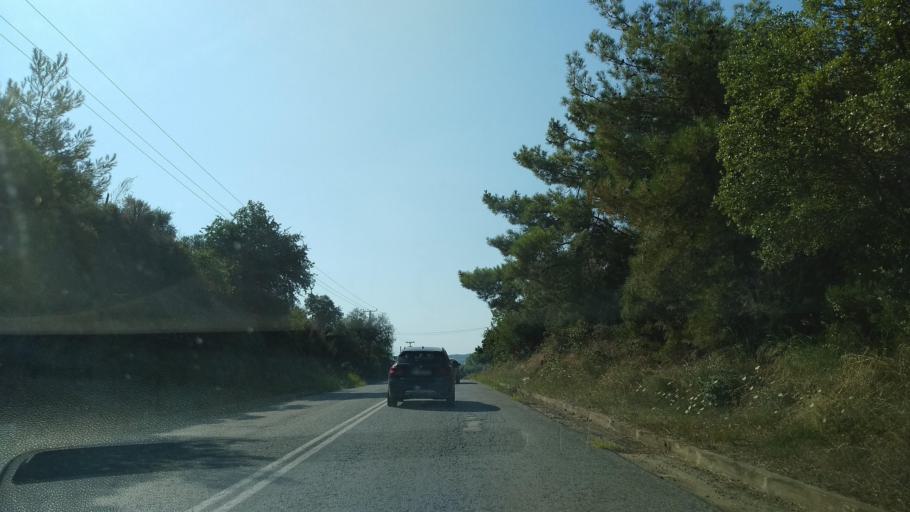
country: GR
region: Central Macedonia
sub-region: Nomos Chalkidikis
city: Ierissos
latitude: 40.4205
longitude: 23.8511
